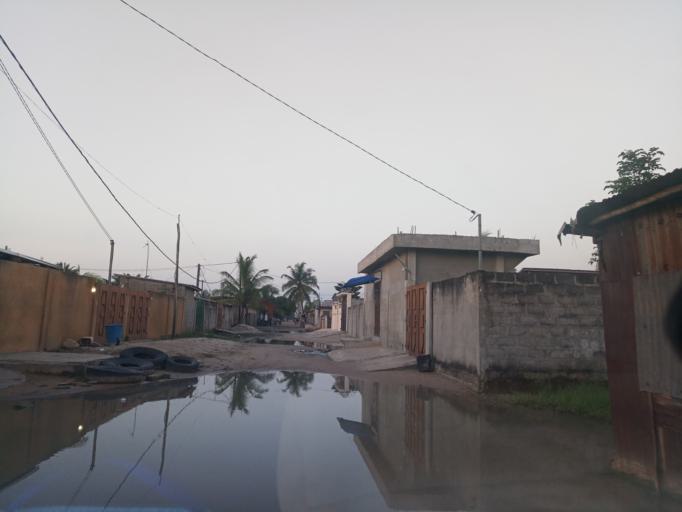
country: BJ
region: Atlantique
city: Hevie
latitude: 6.3890
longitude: 2.2879
